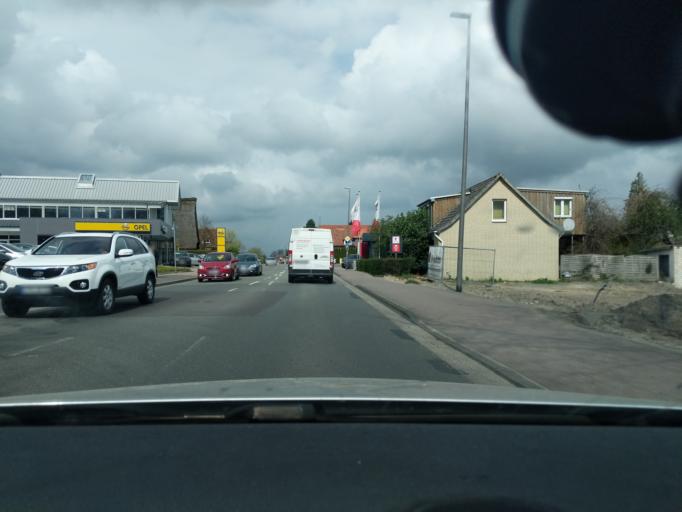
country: DE
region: Lower Saxony
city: Stade
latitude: 53.5897
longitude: 9.4864
